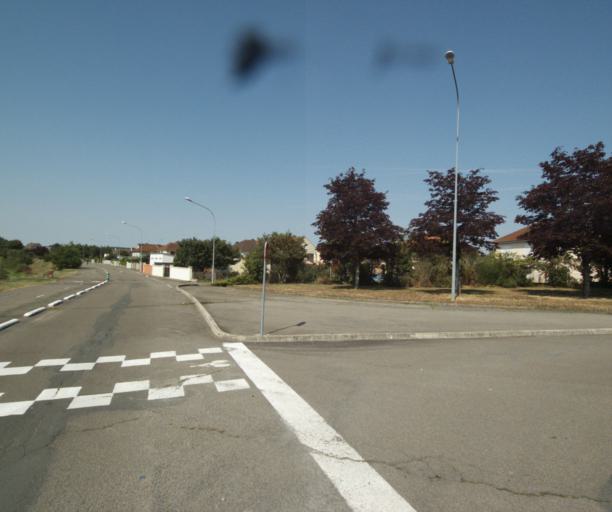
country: FR
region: Bourgogne
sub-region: Departement de Saone-et-Loire
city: Gueugnon
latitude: 46.5976
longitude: 4.0556
